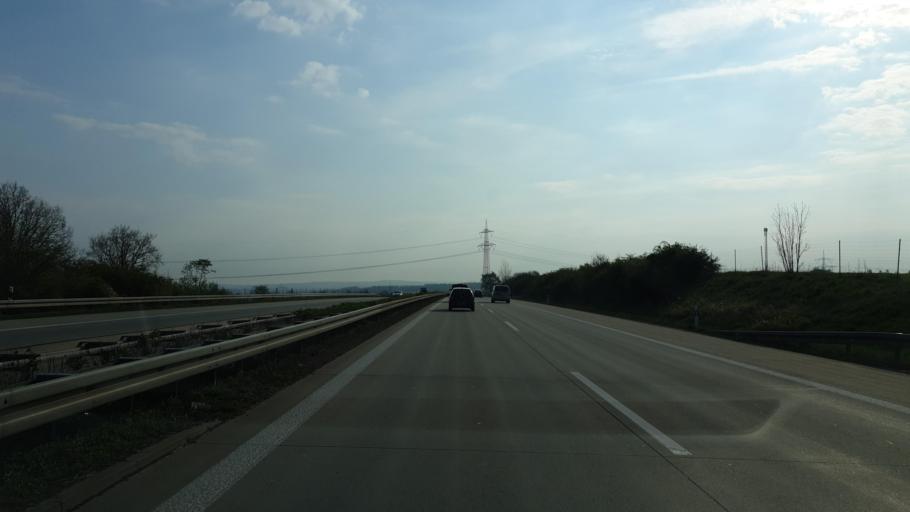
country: DE
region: Saxony
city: Neukirchen
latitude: 50.7932
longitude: 12.8428
